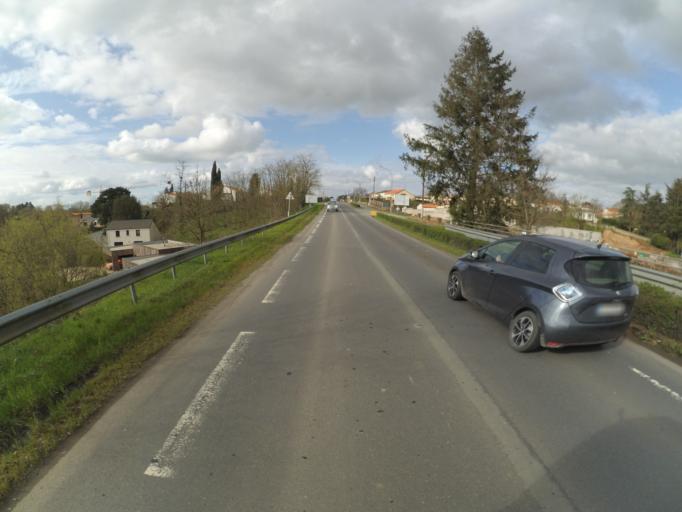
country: FR
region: Pays de la Loire
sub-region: Departement de la Vendee
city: Montaigu
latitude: 46.9656
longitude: -1.3075
